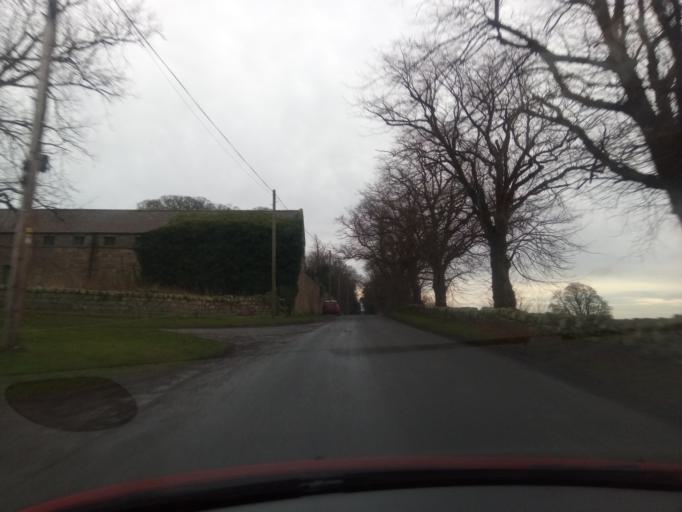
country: GB
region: England
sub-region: Northumberland
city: Whittingham
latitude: 55.4874
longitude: -1.8963
